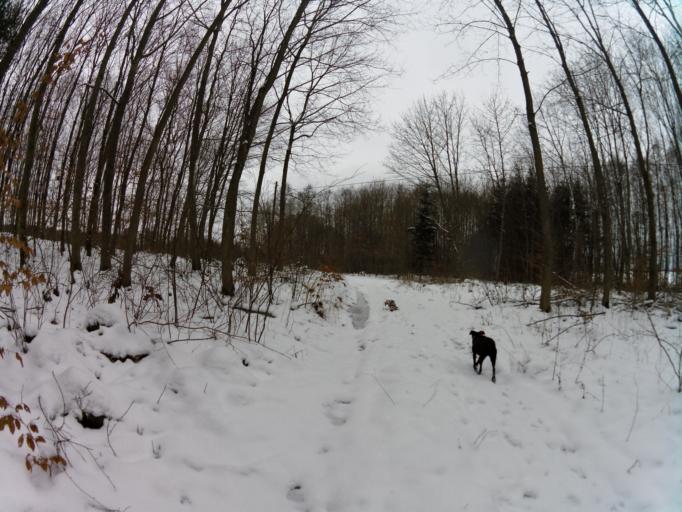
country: PL
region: West Pomeranian Voivodeship
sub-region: Powiat choszczenski
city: Recz
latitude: 53.3322
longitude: 15.5454
